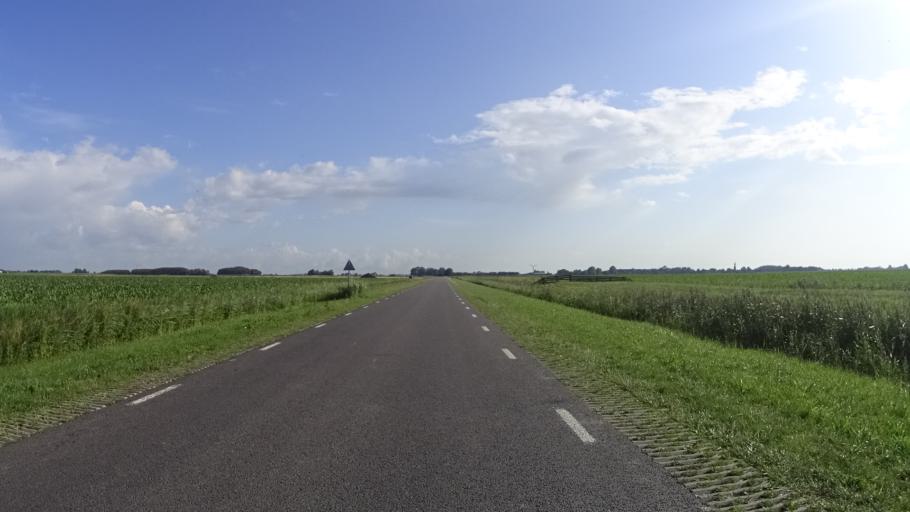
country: NL
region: Friesland
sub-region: Gemeente Harlingen
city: Harlingen
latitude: 53.1226
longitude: 5.4535
